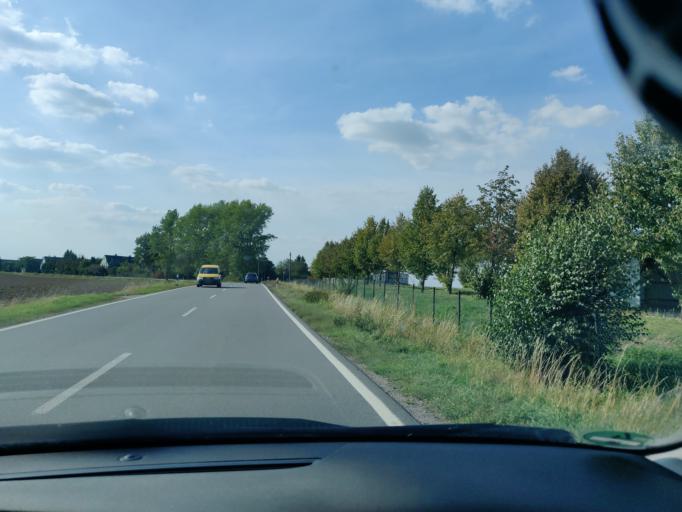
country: DE
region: Saxony
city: Erlau
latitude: 51.0164
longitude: 12.9022
